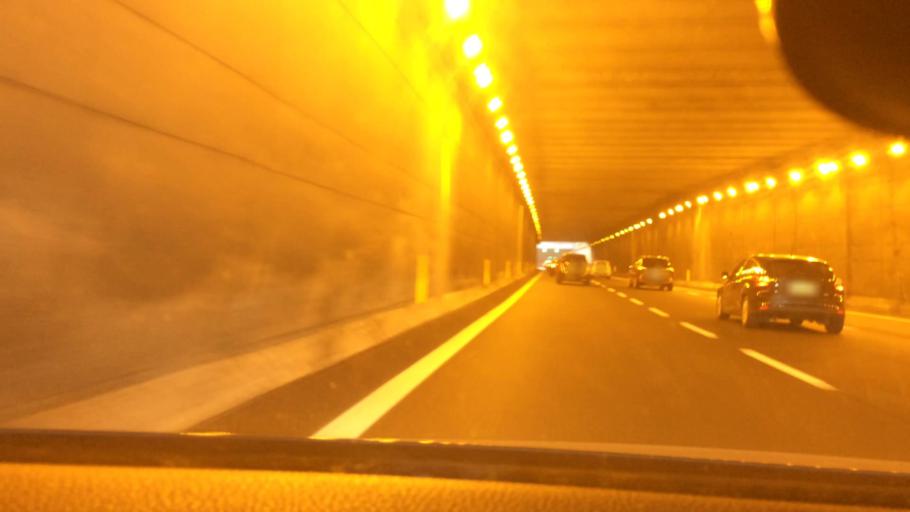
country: IT
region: Lombardy
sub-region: Citta metropolitana di Milano
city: Rho
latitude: 45.5210
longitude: 9.0667
